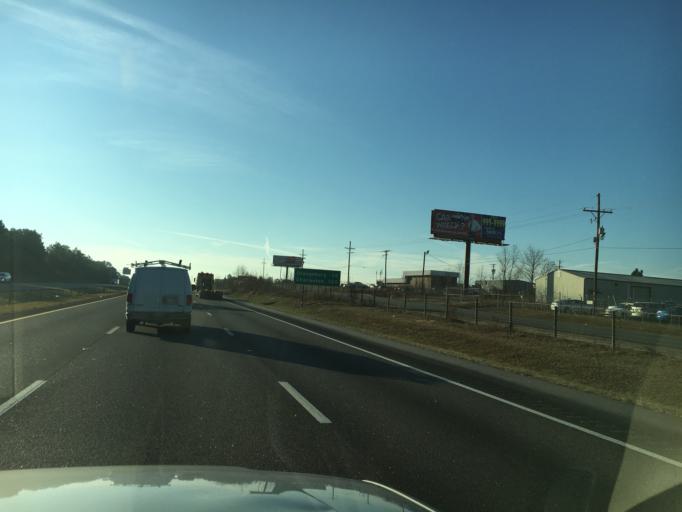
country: US
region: South Carolina
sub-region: Lexington County
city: Pineridge
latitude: 33.8684
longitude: -81.0337
